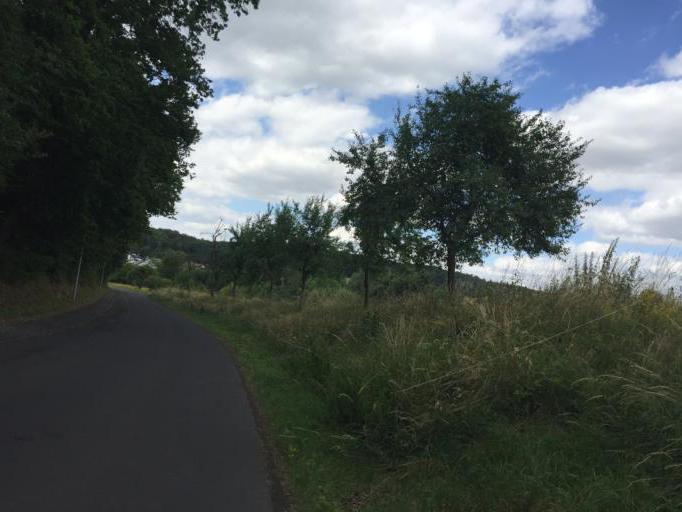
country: DE
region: Hesse
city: Lollar
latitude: 50.6434
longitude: 8.6772
